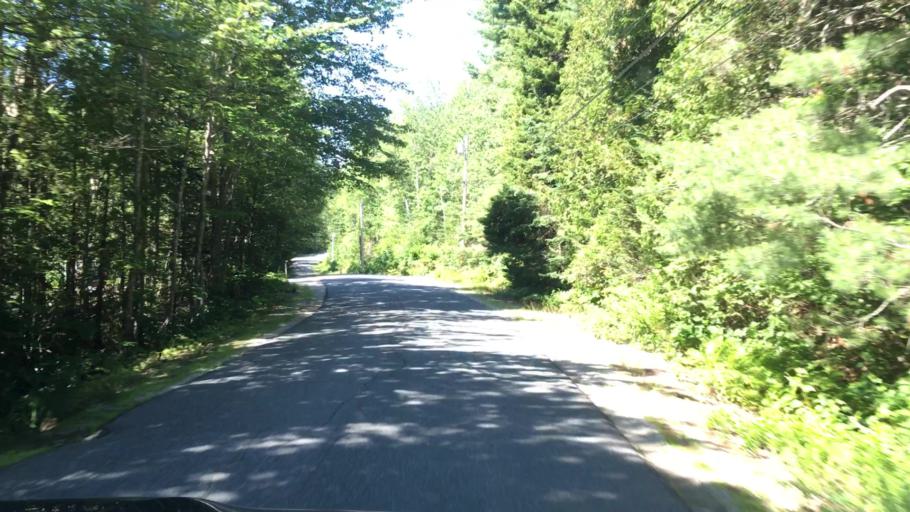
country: US
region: Maine
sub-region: Hancock County
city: Sedgwick
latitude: 44.3169
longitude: -68.6148
